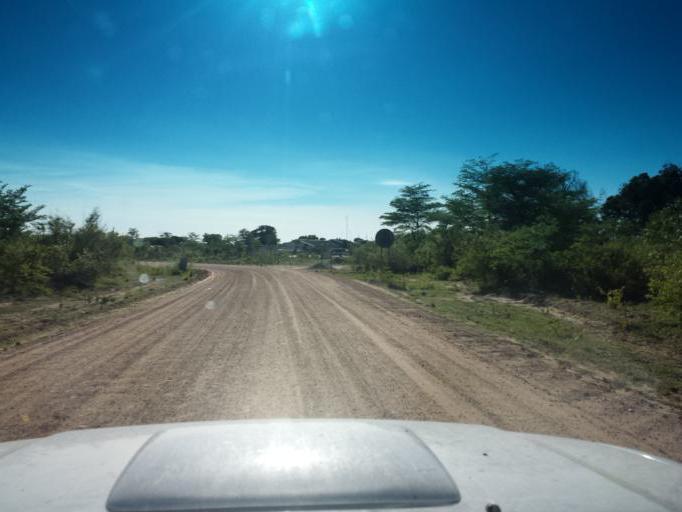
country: BW
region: North West
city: Shakawe
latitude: -18.2569
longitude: 21.7581
